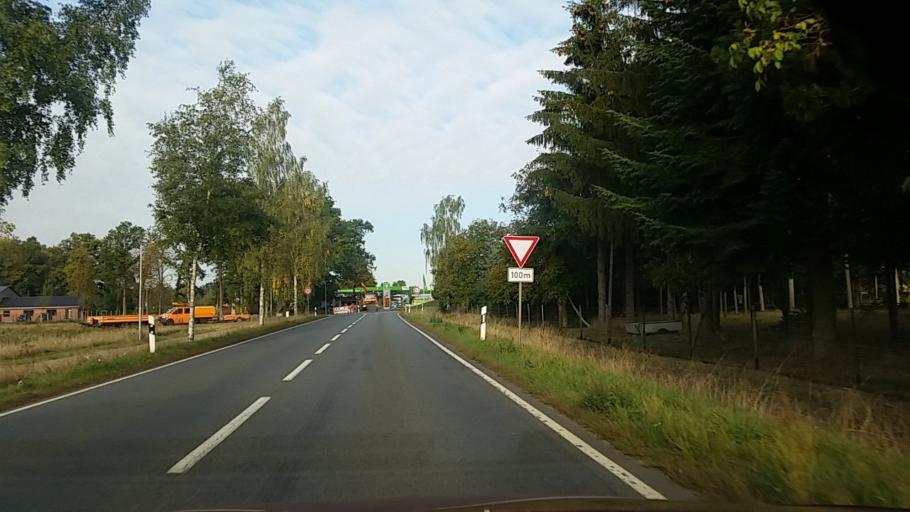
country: DE
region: Lower Saxony
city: Lachendorf
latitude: 52.6321
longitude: 10.2251
